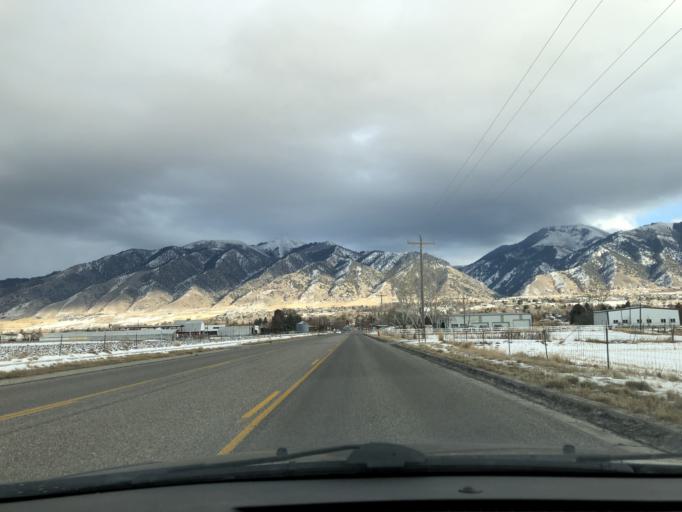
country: US
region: Utah
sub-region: Cache County
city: Providence
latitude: 41.7027
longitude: -111.8398
